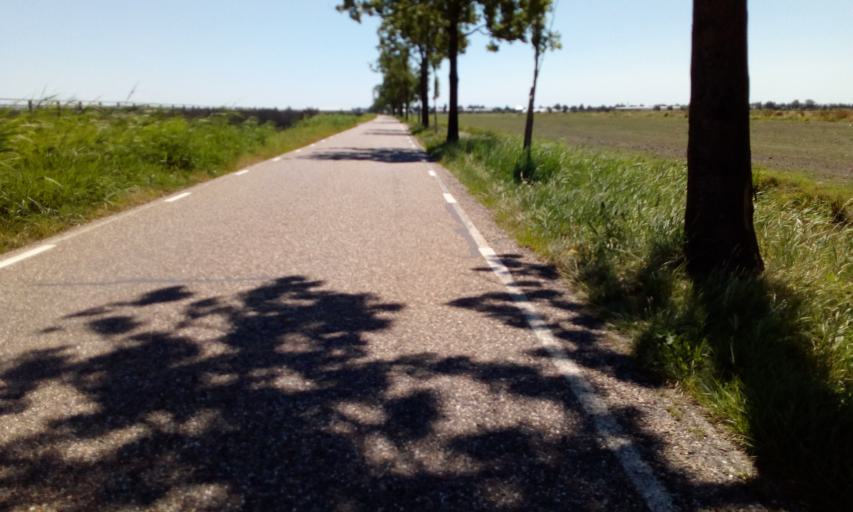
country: NL
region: South Holland
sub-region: Gemeente Alphen aan den Rijn
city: Alphen aan den Rijn
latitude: 52.1030
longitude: 4.6869
